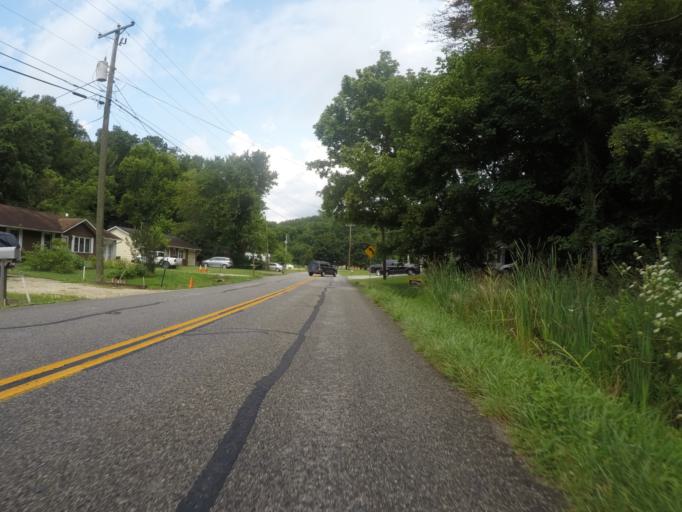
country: US
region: Kentucky
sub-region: Boyd County
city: Meads
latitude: 38.4146
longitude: -82.6827
